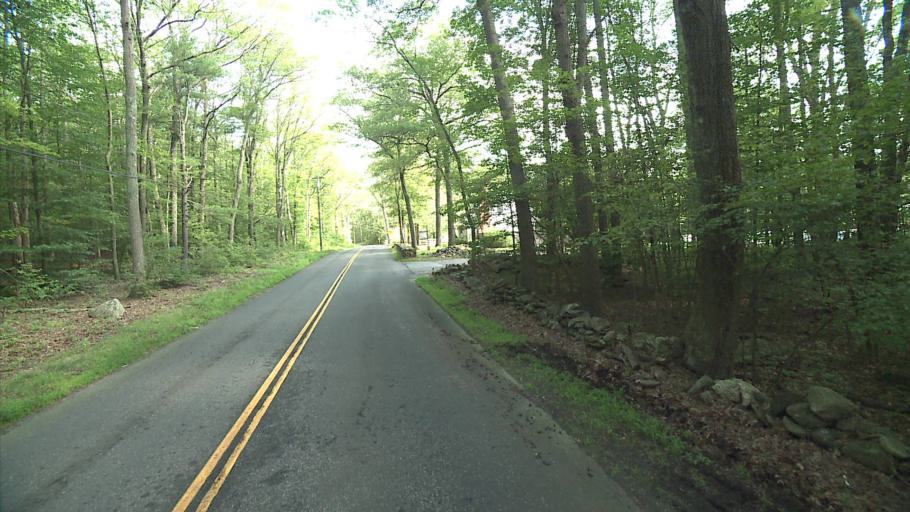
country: US
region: Connecticut
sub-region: Middlesex County
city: Chester Center
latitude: 41.3659
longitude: -72.4949
